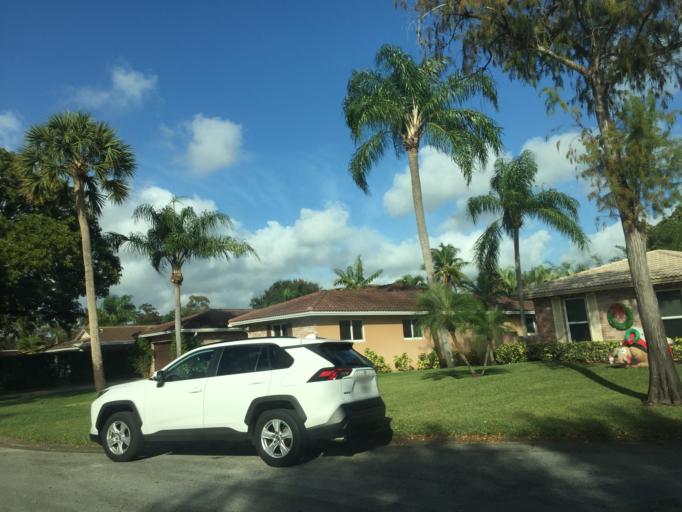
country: US
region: Florida
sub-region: Broward County
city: North Lauderdale
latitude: 26.2382
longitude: -80.2346
